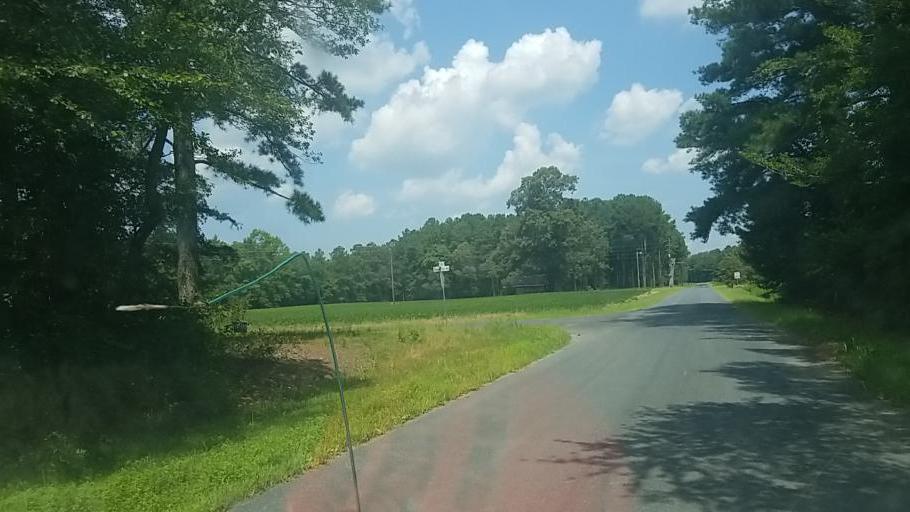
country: US
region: Maryland
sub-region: Wicomico County
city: Pittsville
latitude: 38.2867
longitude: -75.4785
